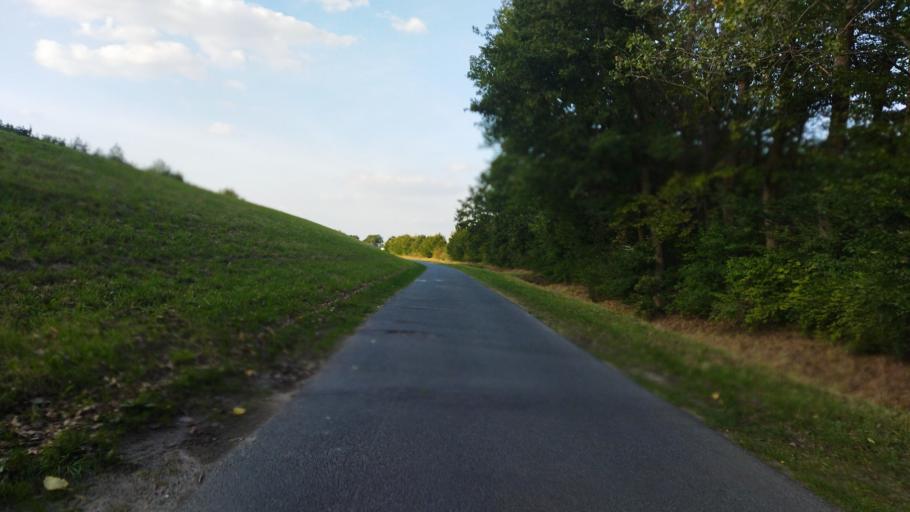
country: DE
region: Lower Saxony
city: Lehe
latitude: 53.0435
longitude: 7.3197
